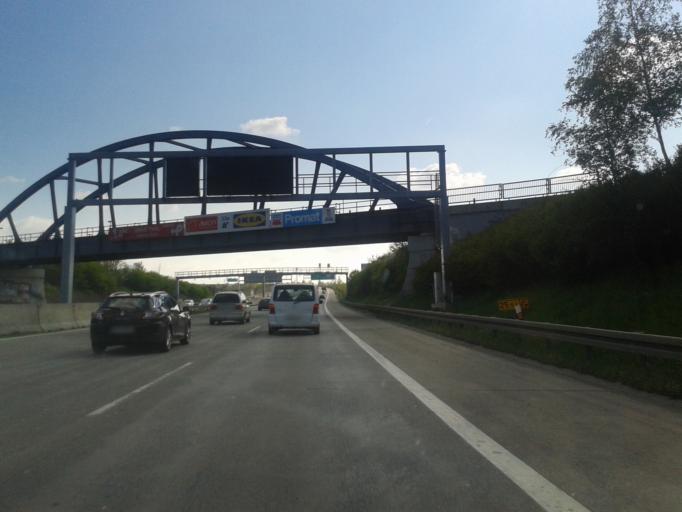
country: CZ
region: Central Bohemia
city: Hostivice
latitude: 50.0696
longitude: 14.2841
